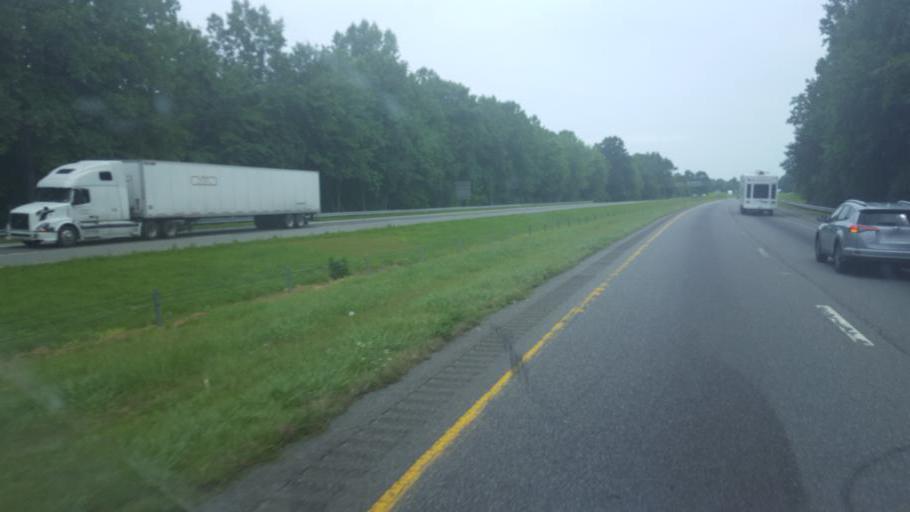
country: US
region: North Carolina
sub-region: Iredell County
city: Statesville
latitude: 35.8612
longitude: -80.8639
